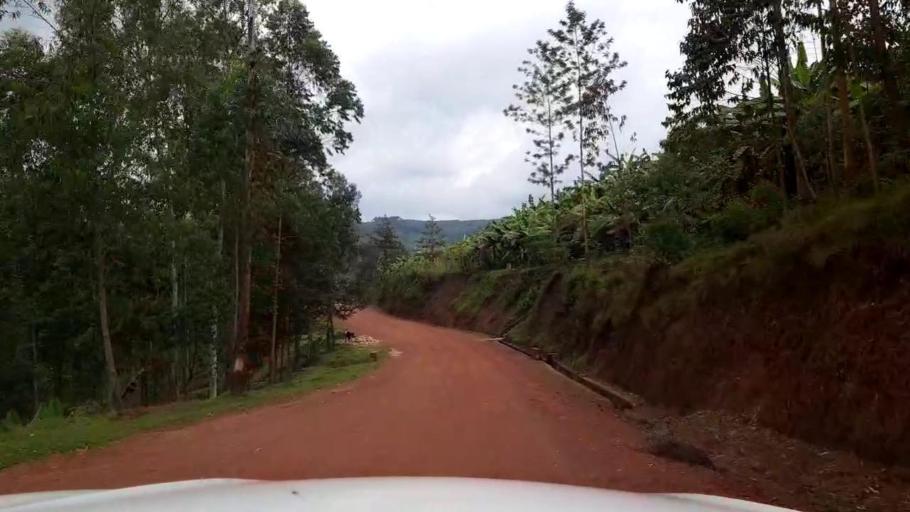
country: RW
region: Northern Province
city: Musanze
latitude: -1.6603
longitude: 29.8005
